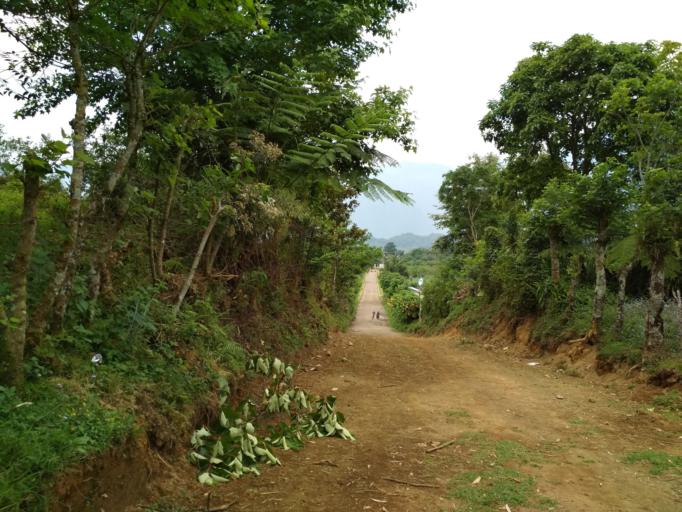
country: MX
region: Veracruz
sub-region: Mariano Escobedo
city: Mariano Escobedo
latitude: 18.9197
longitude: -97.1269
